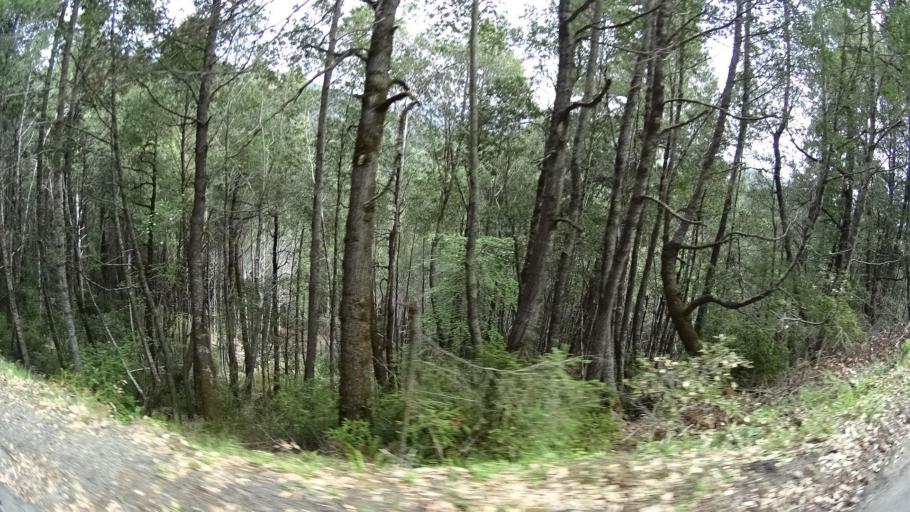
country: US
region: California
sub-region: Humboldt County
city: Redway
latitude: 40.0648
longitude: -123.8292
